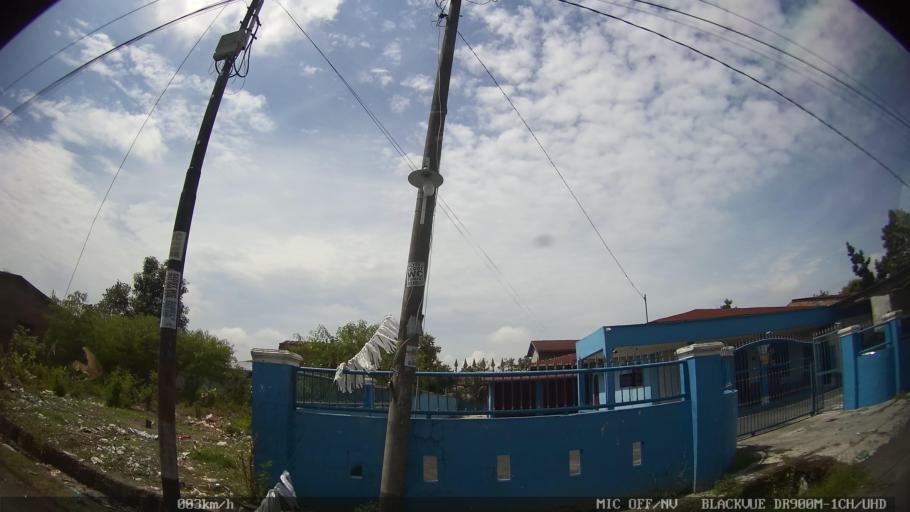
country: ID
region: North Sumatra
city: Medan
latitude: 3.6022
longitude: 98.7499
